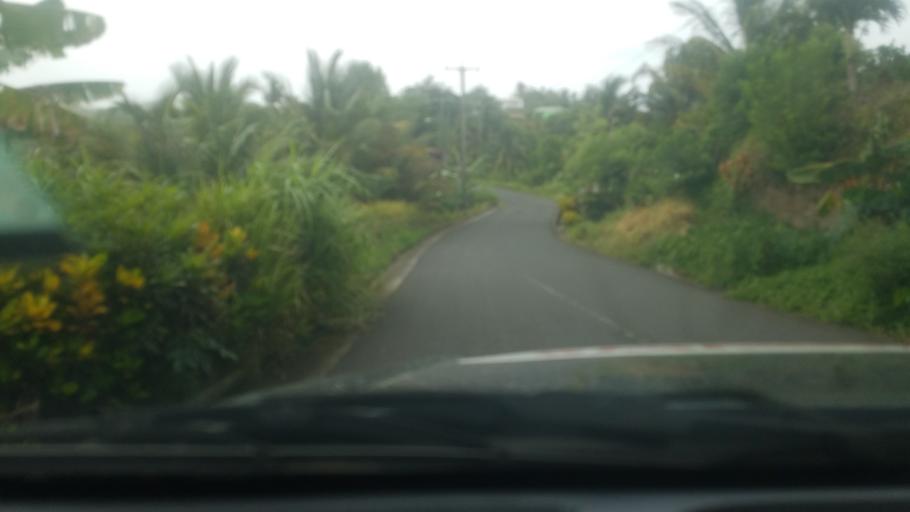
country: LC
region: Laborie Quarter
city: Laborie
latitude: 13.7728
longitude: -60.9922
